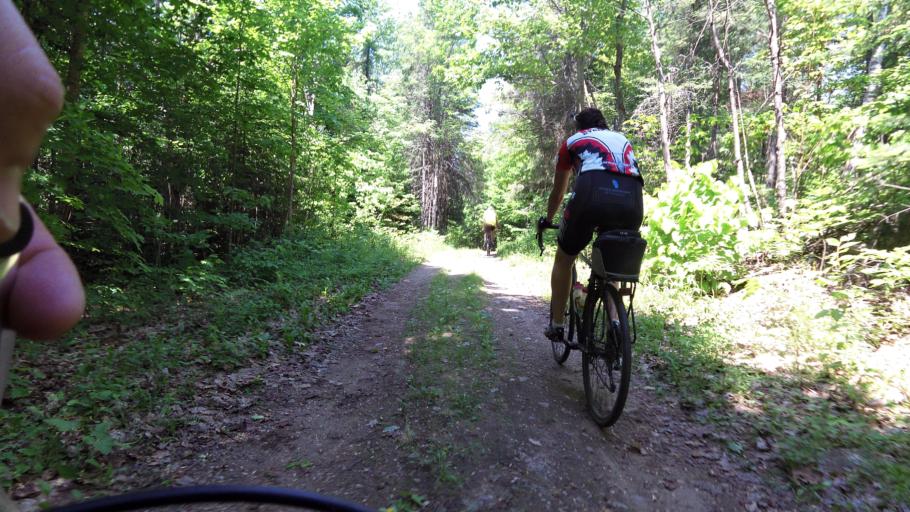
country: CA
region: Quebec
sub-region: Outaouais
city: Wakefield
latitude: 45.5679
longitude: -75.9144
